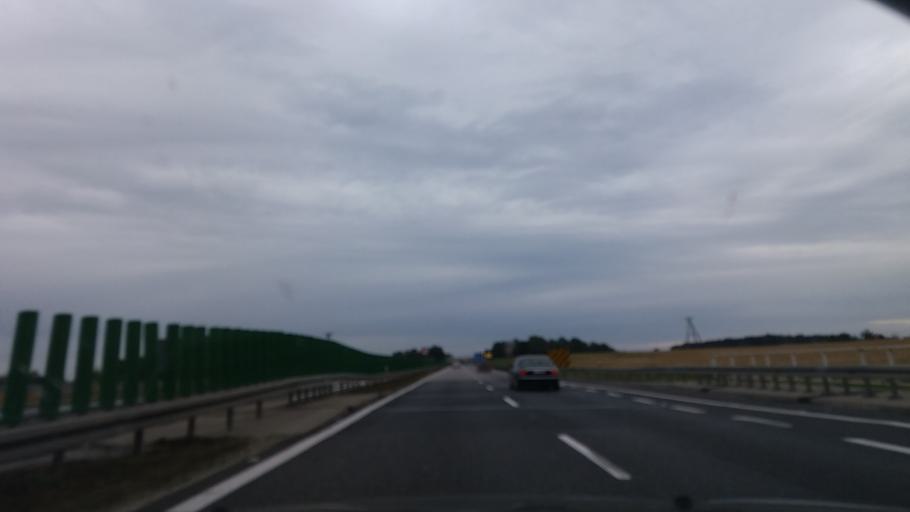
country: PL
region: Lower Silesian Voivodeship
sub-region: Powiat sredzki
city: Udanin
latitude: 51.0873
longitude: 16.4169
